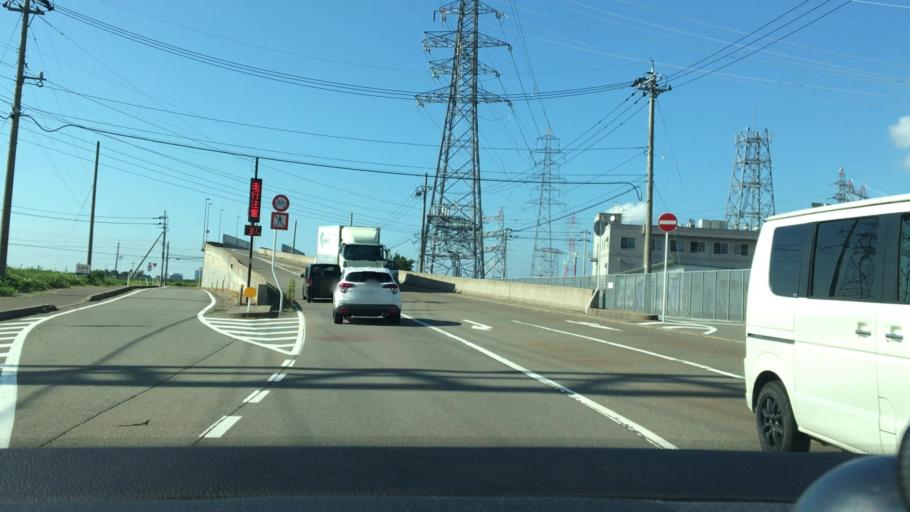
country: JP
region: Fukui
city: Maruoka
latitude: 36.0902
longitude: 136.2823
